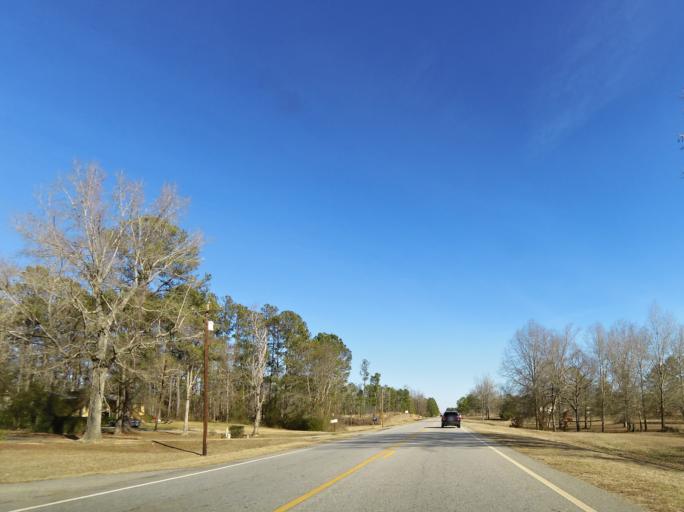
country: US
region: Georgia
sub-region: Crawford County
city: Roberta
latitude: 32.7527
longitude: -84.1916
